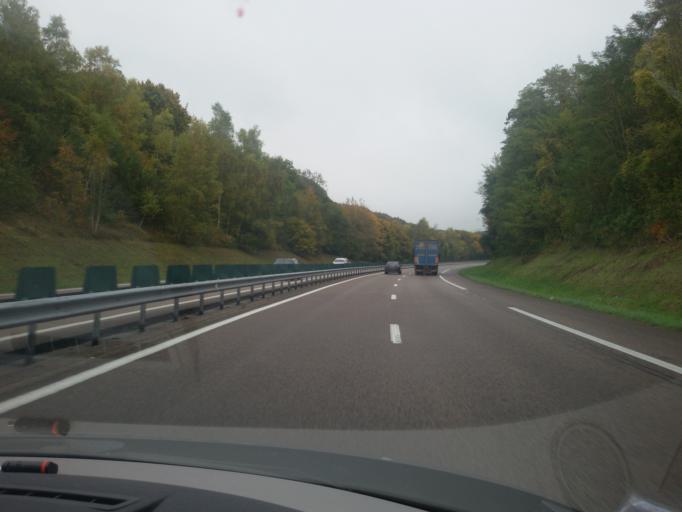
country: FR
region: Haute-Normandie
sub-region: Departement de l'Eure
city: Toutainville
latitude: 49.3787
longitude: 0.4890
